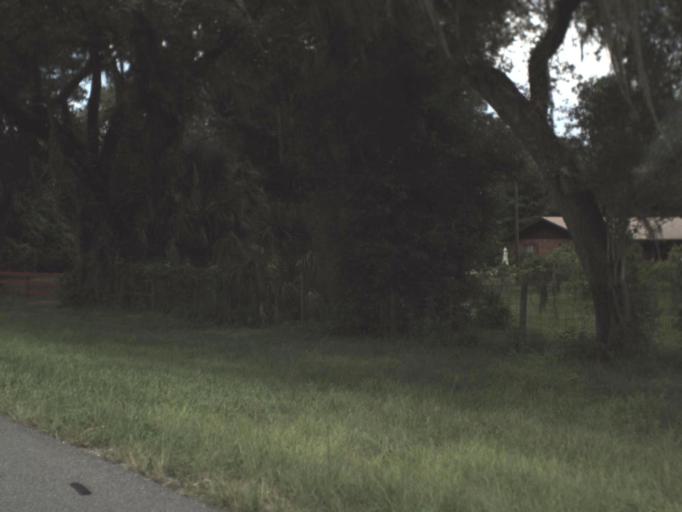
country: US
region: Florida
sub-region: Pasco County
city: Lacoochee
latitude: 28.4806
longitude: -82.1962
